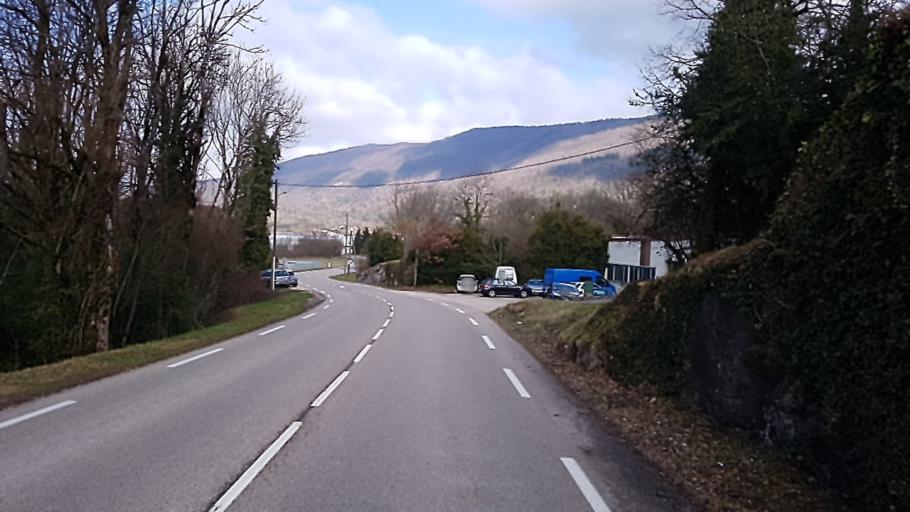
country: FR
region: Rhone-Alpes
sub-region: Departement de l'Ain
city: Dortan
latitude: 46.3232
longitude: 5.6669
